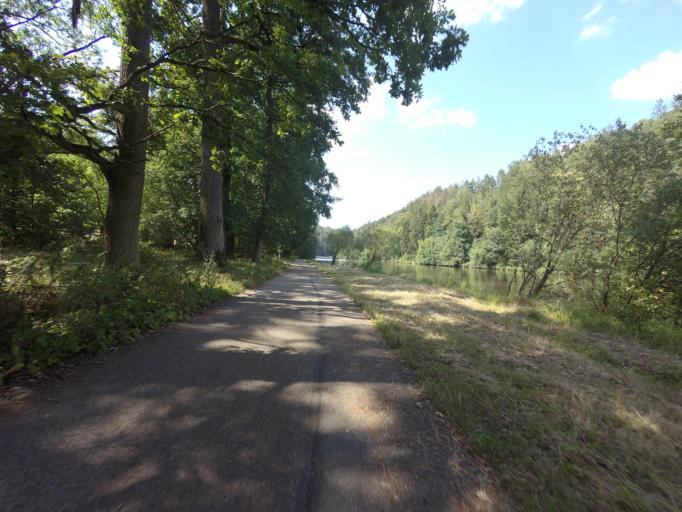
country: CZ
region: Jihocesky
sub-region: Okres Ceske Budejovice
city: Hluboka nad Vltavou
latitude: 49.0693
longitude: 14.4605
